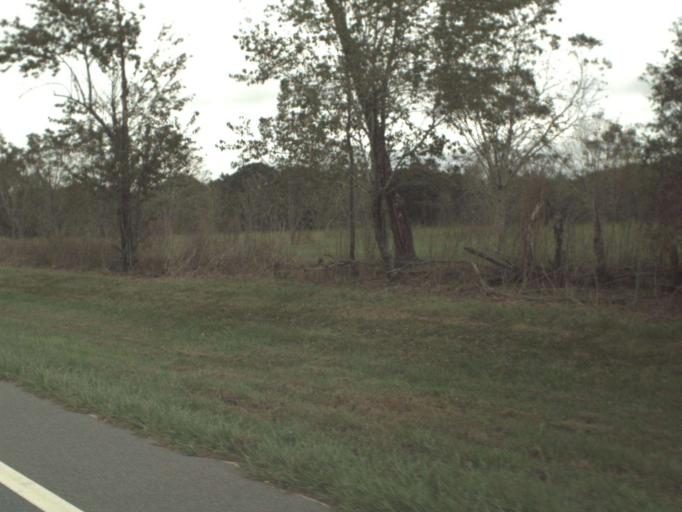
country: US
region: Florida
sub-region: Jackson County
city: Sneads
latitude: 30.7528
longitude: -85.0194
